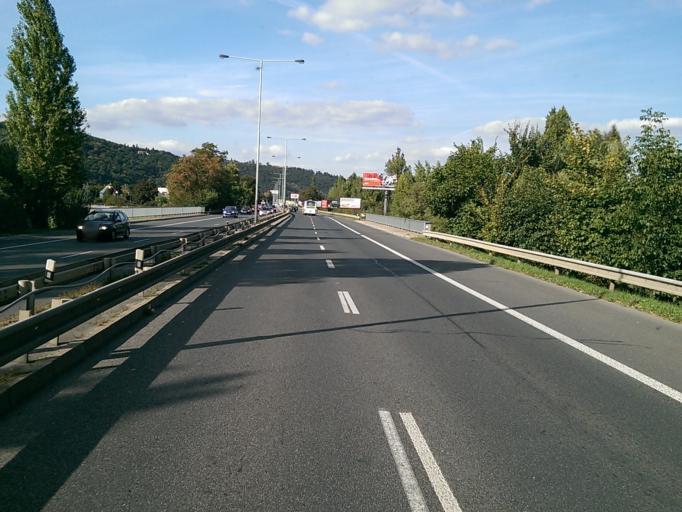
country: CZ
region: Praha
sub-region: Praha 12
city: Modrany
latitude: 50.0086
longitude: 14.3948
